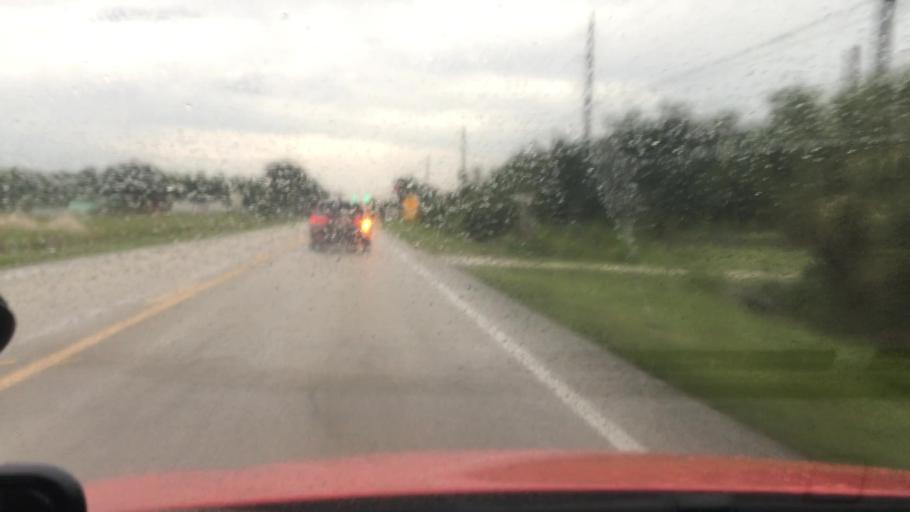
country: US
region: Florida
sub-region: Volusia County
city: Samsula-Spruce Creek
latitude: 29.0809
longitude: -81.0683
